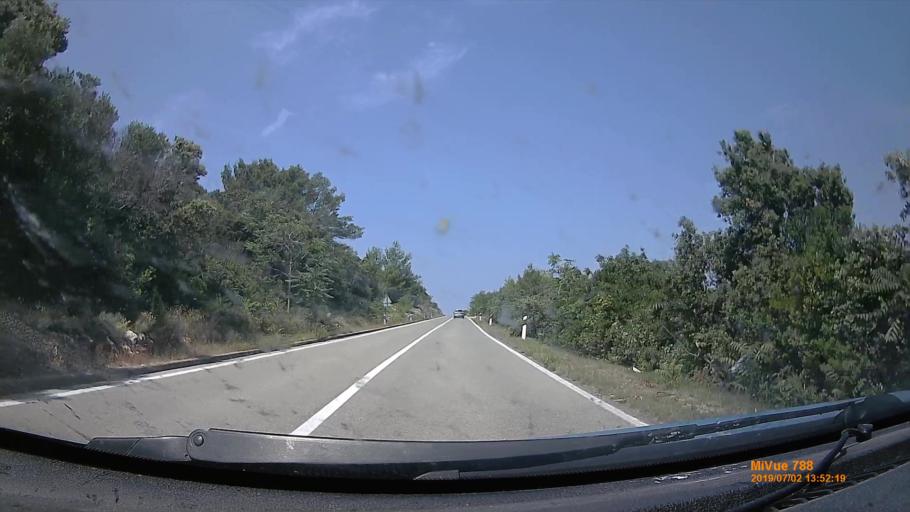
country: HR
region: Primorsko-Goranska
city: Mali Losinj
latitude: 44.6126
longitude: 14.3974
